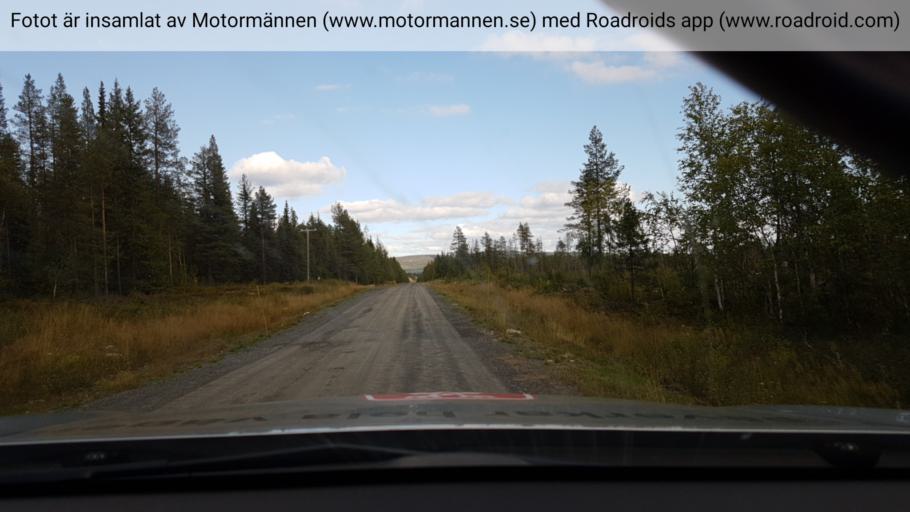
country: SE
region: Vaesterbotten
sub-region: Sorsele Kommun
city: Sorsele
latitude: 65.4574
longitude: 17.7337
